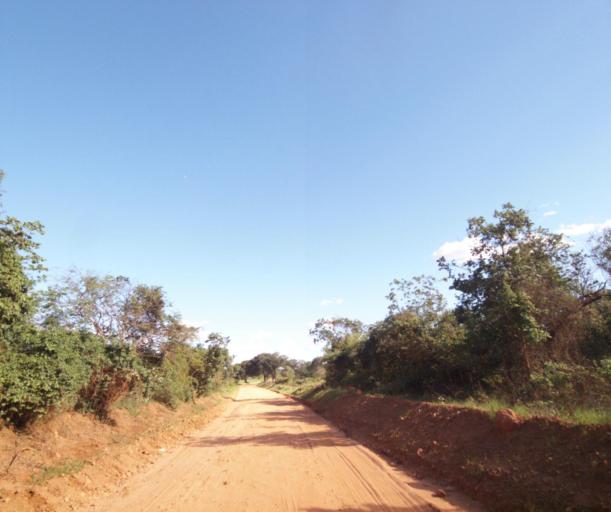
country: BR
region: Bahia
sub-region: Carinhanha
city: Carinhanha
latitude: -14.2150
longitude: -44.5375
